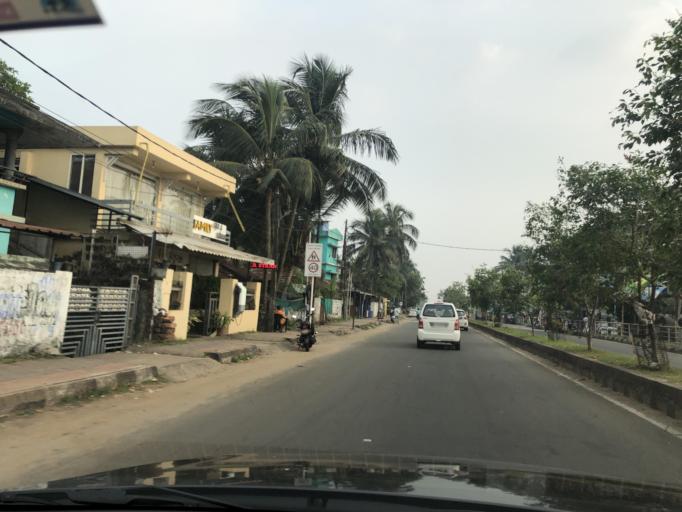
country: IN
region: Kerala
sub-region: Kozhikode
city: Kozhikode
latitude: 11.2742
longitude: 75.7645
